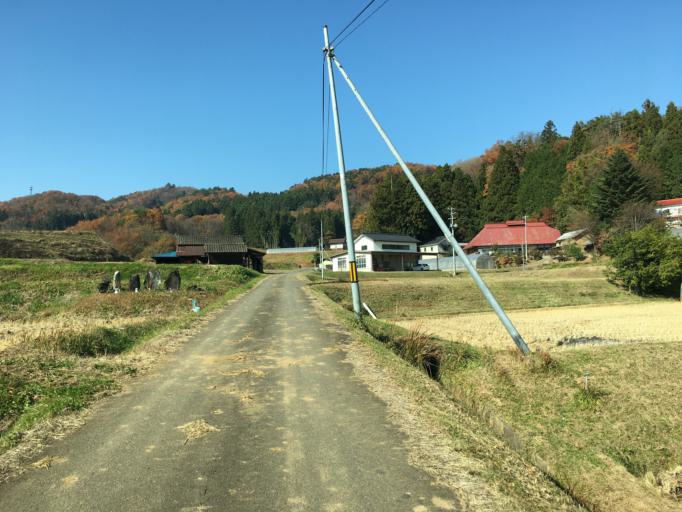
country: JP
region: Fukushima
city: Nihommatsu
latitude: 37.5746
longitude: 140.3768
